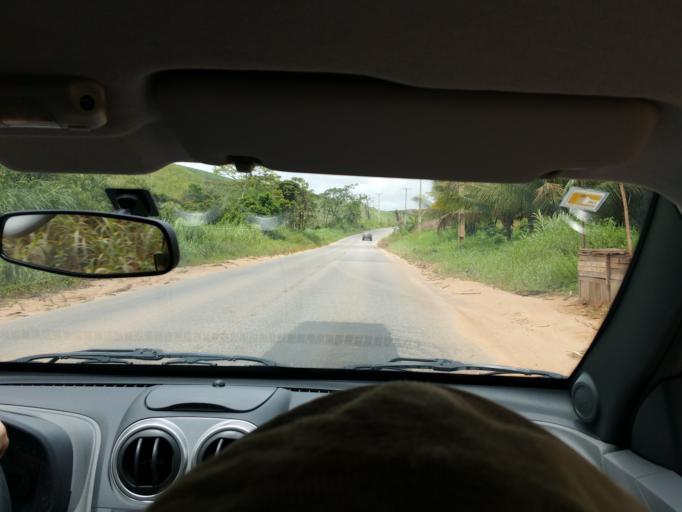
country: BR
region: Pernambuco
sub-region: Sirinhaem
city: Sirinhaem
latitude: -8.6238
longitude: -35.1249
